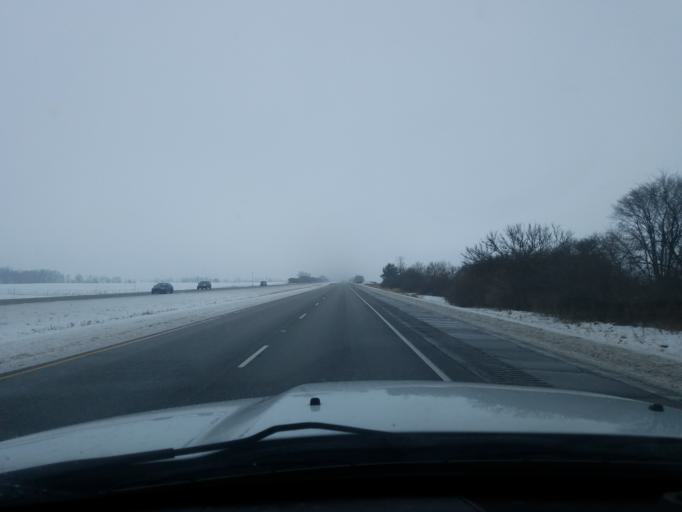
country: US
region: Indiana
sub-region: Fulton County
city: Rochester
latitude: 40.9786
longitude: -86.1678
